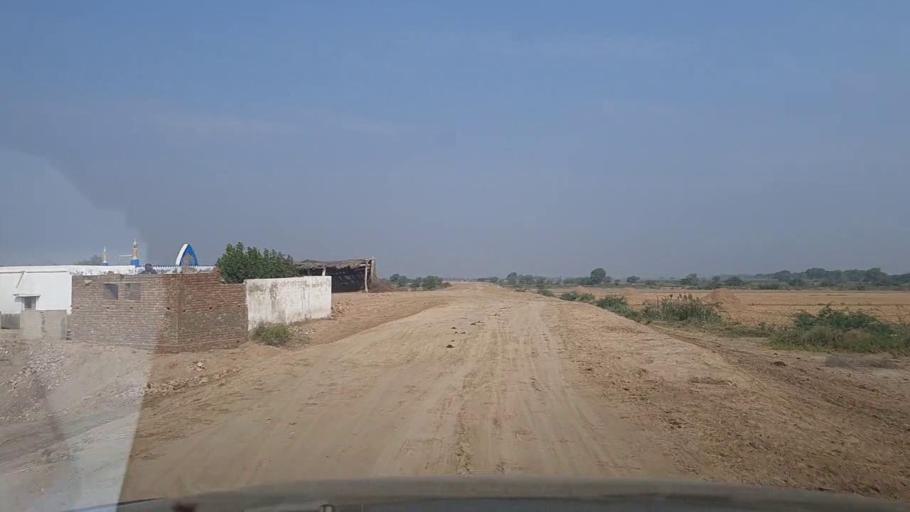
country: PK
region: Sindh
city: Bulri
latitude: 25.0029
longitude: 68.2882
